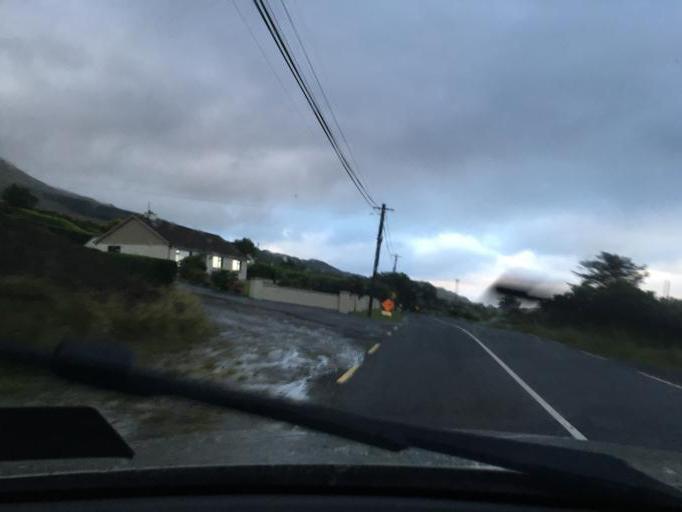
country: IE
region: Ulster
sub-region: County Donegal
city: Killybegs
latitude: 54.6296
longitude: -8.5194
